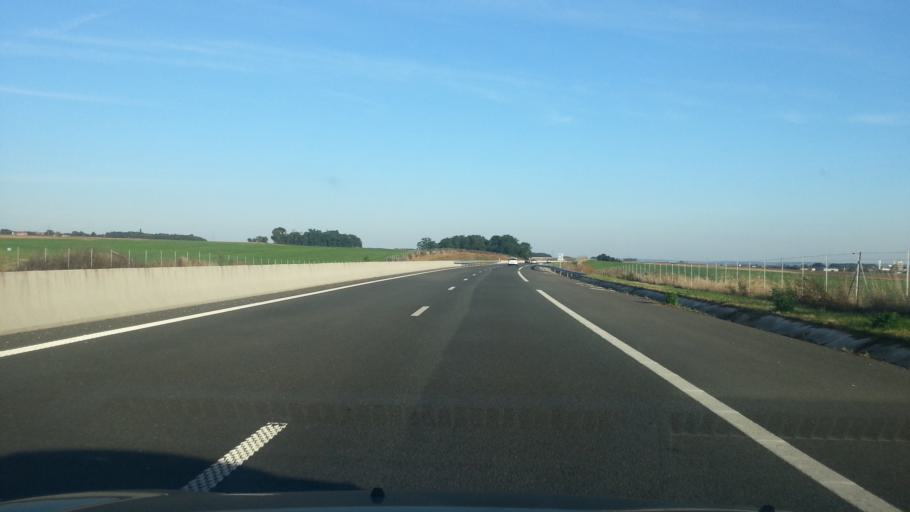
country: FR
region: Picardie
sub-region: Departement de l'Oise
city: Catenoy
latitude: 49.3848
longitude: 2.4938
